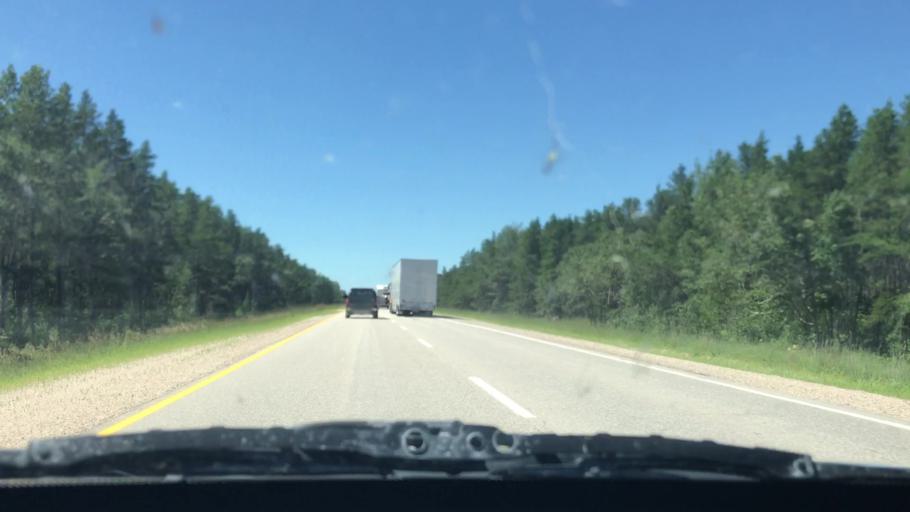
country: CA
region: Manitoba
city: La Broquerie
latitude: 49.6576
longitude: -96.2006
